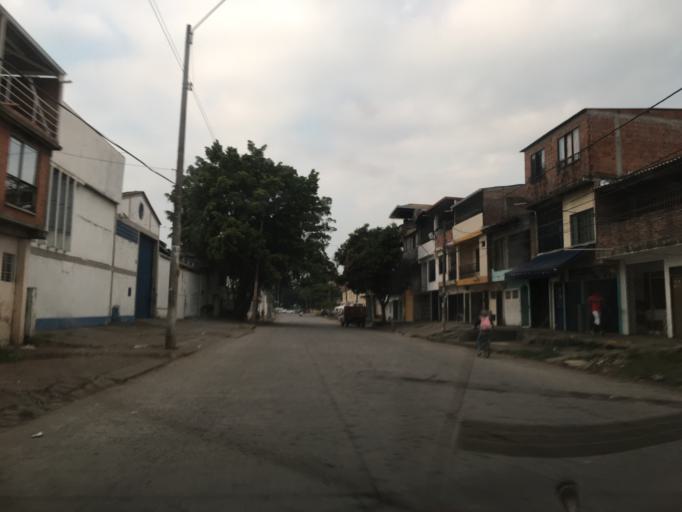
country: CO
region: Valle del Cauca
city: Cali
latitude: 3.4210
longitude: -76.5218
